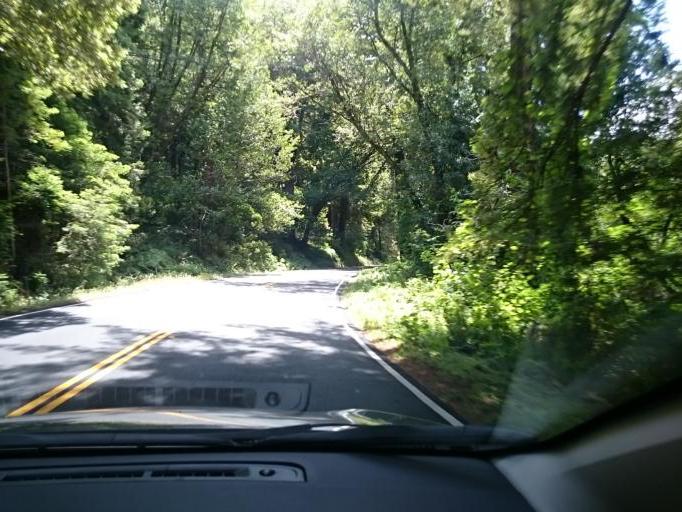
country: US
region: California
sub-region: Mendocino County
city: Fort Bragg
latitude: 39.1863
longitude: -123.7173
